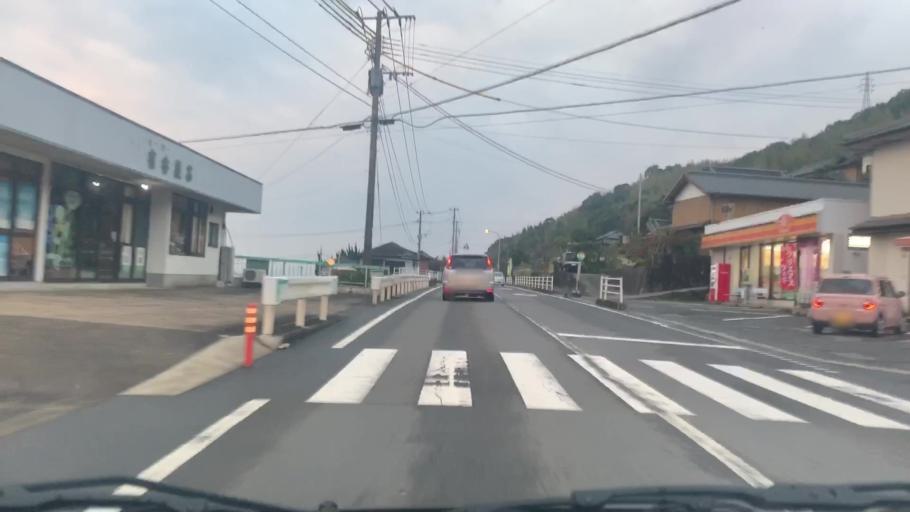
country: JP
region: Saga Prefecture
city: Ureshinomachi-shimojuku
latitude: 33.0516
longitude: 129.9278
